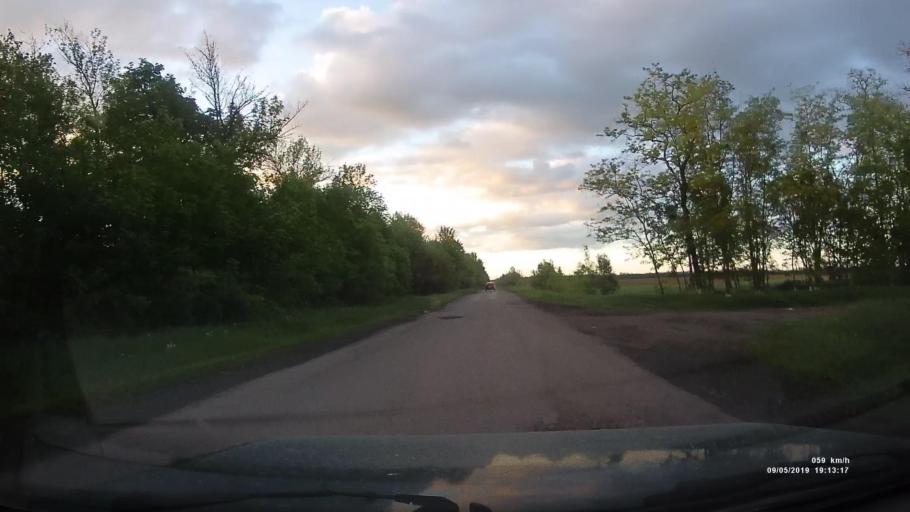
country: RU
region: Krasnodarskiy
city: Kanelovskaya
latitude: 46.7492
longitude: 39.2137
